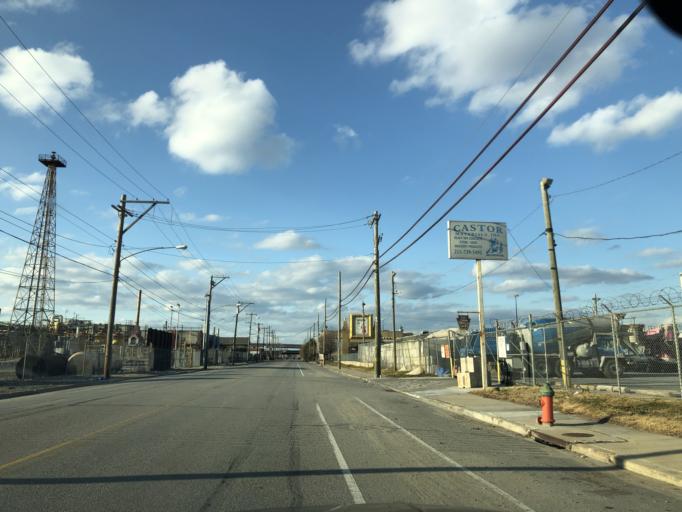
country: US
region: New Jersey
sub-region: Camden County
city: Pennsauken
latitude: 39.9842
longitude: -75.0852
